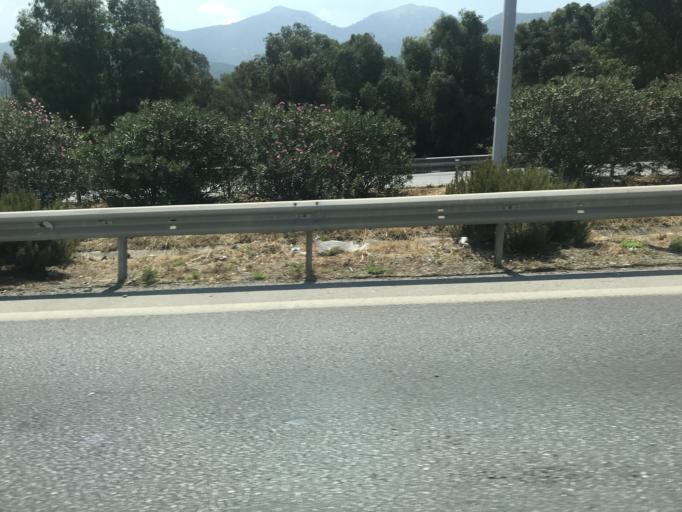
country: TR
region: Izmir
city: Karsiyaka
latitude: 38.3883
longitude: 26.9484
